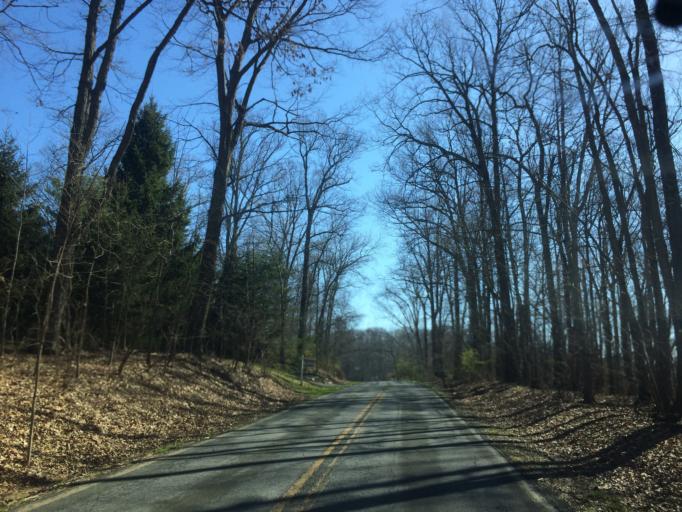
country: US
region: Maryland
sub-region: Carroll County
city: Manchester
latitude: 39.6882
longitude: -76.9670
